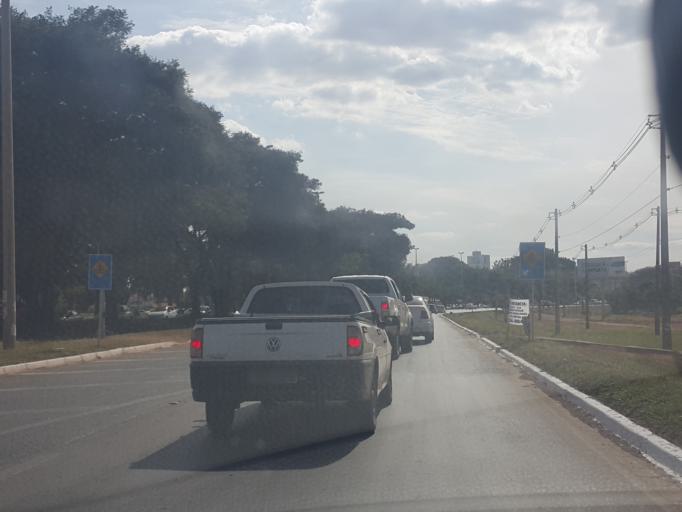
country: BR
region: Federal District
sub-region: Brasilia
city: Brasilia
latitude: -15.8301
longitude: -48.0509
